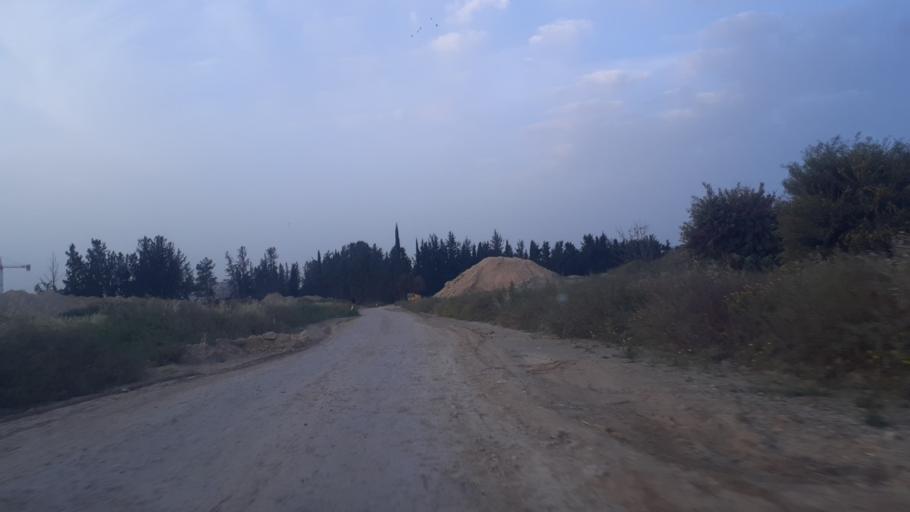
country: CY
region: Limassol
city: Ypsonas
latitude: 34.6681
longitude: 32.9853
